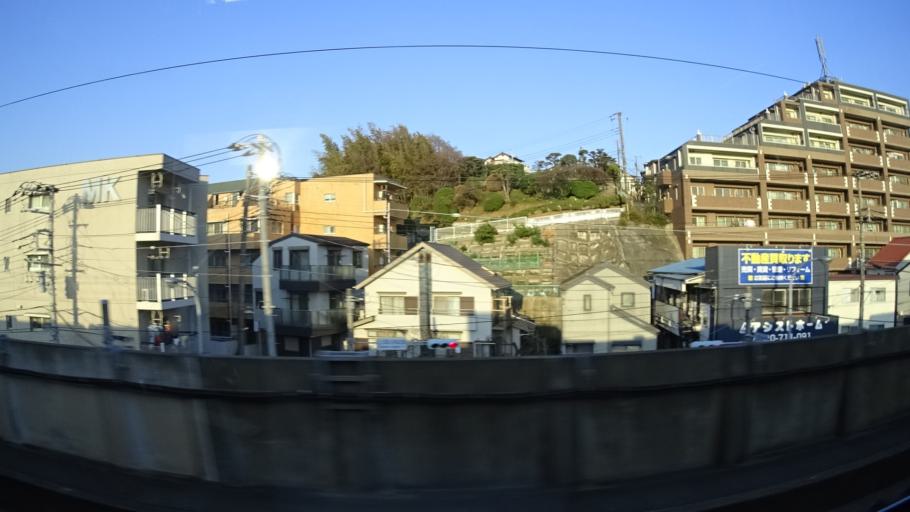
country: JP
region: Kanagawa
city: Yokohama
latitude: 35.4032
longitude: 139.5980
